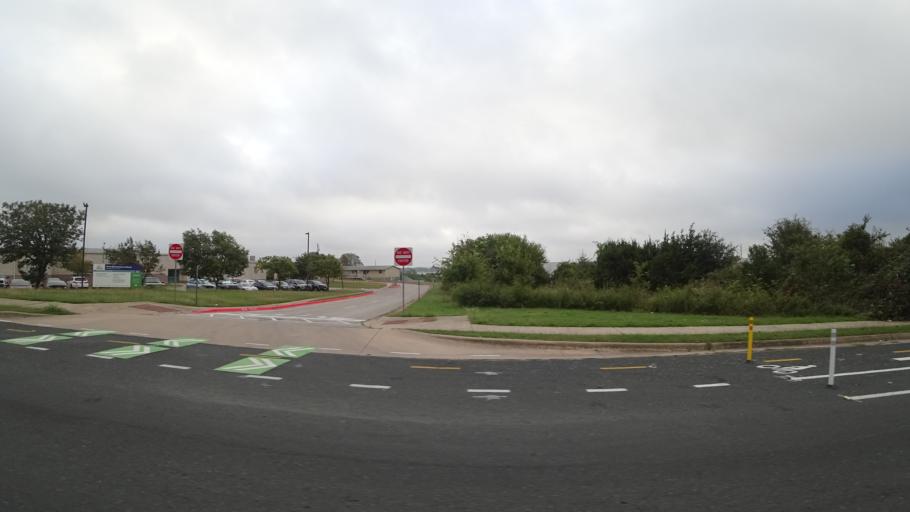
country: US
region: Texas
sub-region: Travis County
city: Austin
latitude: 30.3416
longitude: -97.6897
